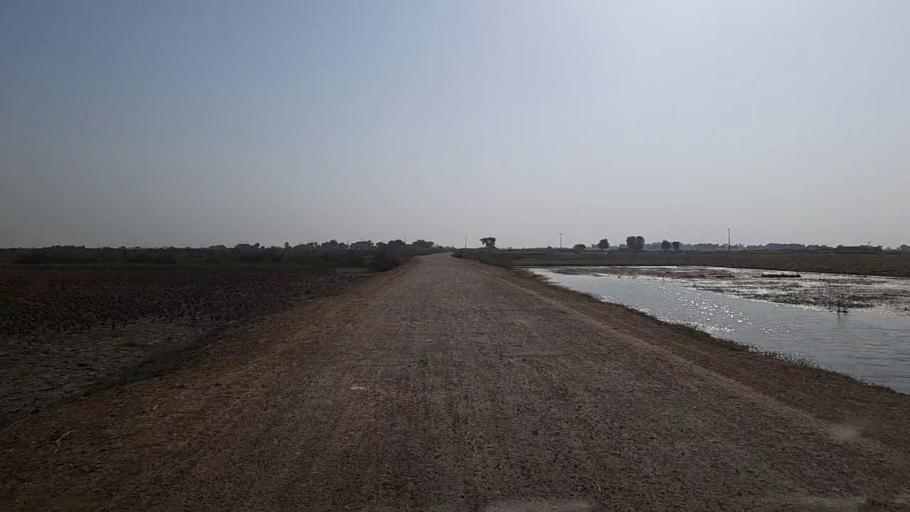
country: PK
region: Sindh
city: Kandhkot
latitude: 28.3856
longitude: 69.3371
